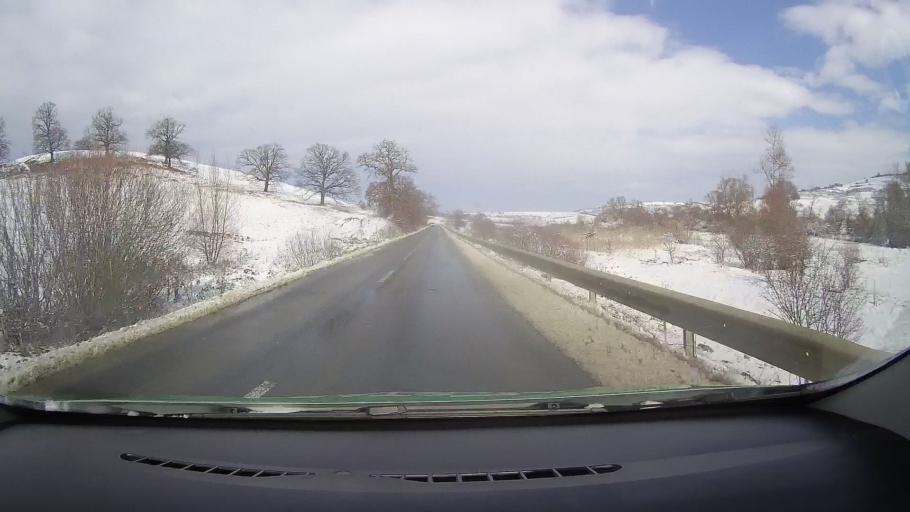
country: RO
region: Sibiu
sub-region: Comuna Altina
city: Altina
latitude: 45.9521
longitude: 24.4527
